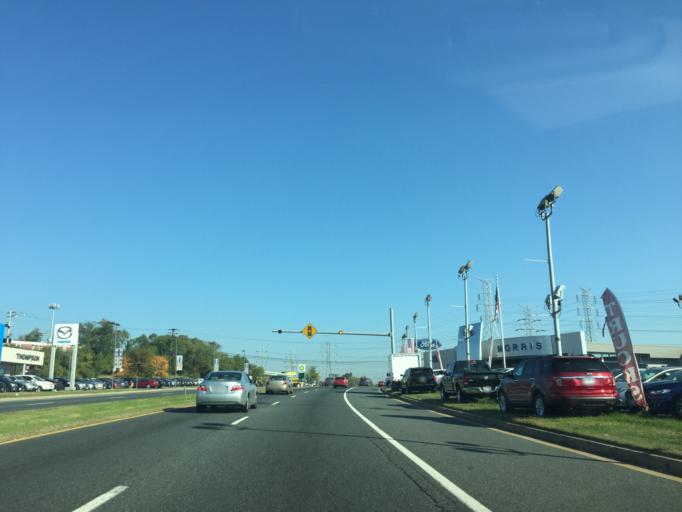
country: US
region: Maryland
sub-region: Baltimore County
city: Rosedale
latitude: 39.2852
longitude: -76.5062
